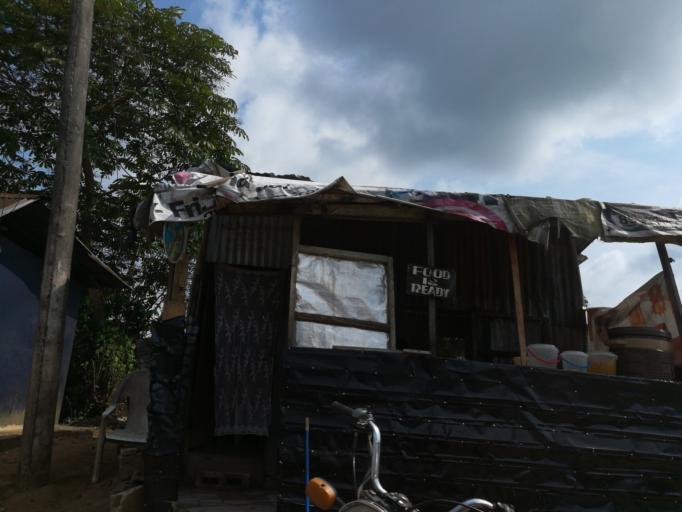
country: NG
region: Rivers
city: Okrika
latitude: 4.7440
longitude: 7.1139
